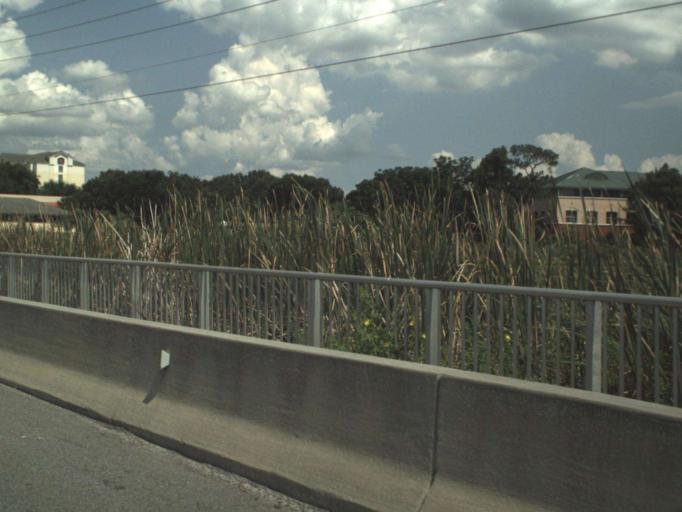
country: US
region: Florida
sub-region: Lake County
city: Tavares
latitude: 28.8217
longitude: -81.7170
